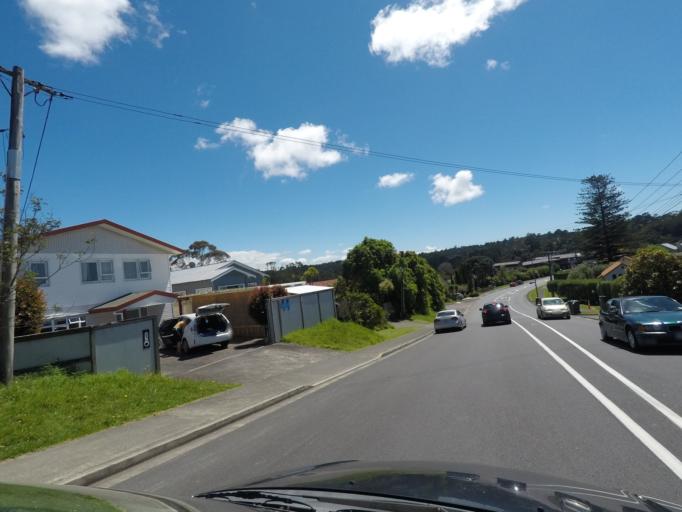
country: NZ
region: Auckland
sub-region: Auckland
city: Rothesay Bay
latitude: -36.7261
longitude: 174.6881
